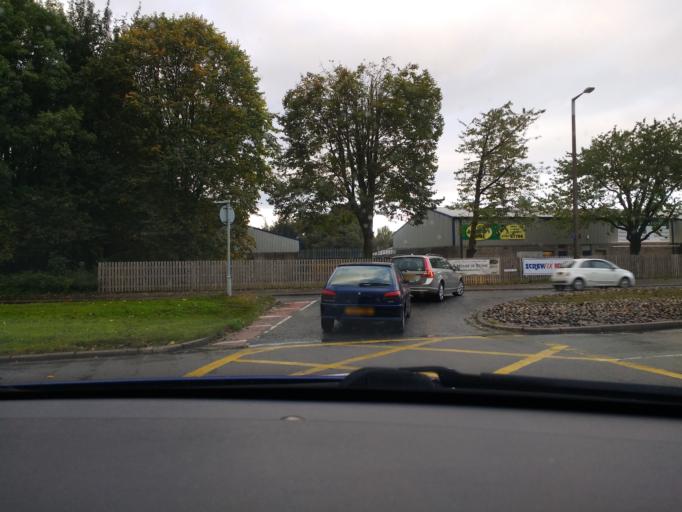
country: GB
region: England
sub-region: Lancashire
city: Lancaster
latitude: 54.0555
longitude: -2.7925
